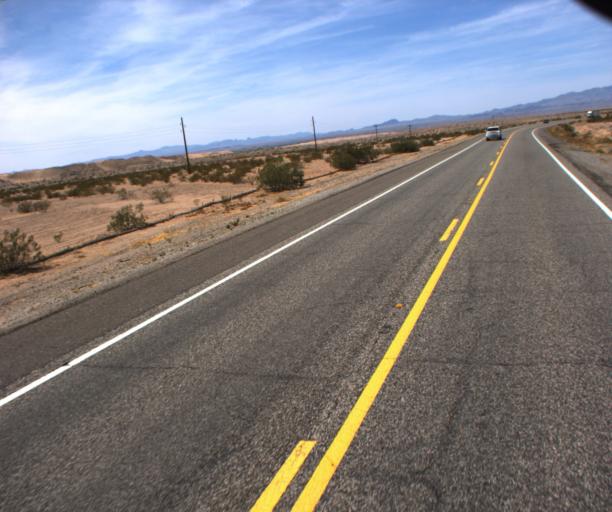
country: US
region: Arizona
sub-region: La Paz County
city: Parker
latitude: 34.0289
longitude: -114.2564
